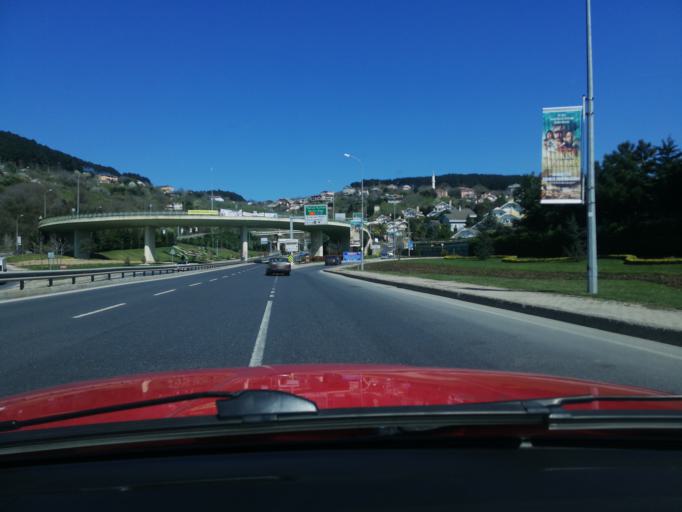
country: TR
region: Istanbul
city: Mahmut Sevket Pasa
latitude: 41.1206
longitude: 29.1285
